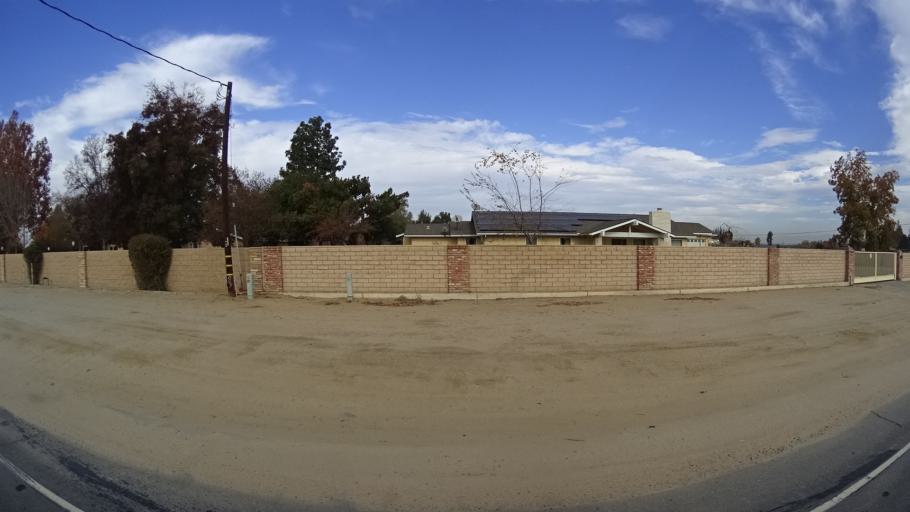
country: US
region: California
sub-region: Kern County
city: Rosedale
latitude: 35.4270
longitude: -119.1370
